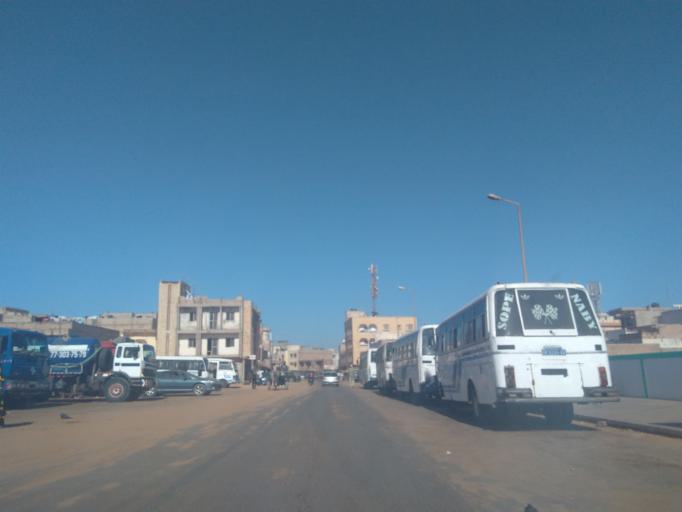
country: SN
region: Dakar
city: Pikine
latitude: 14.7707
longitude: -17.4255
